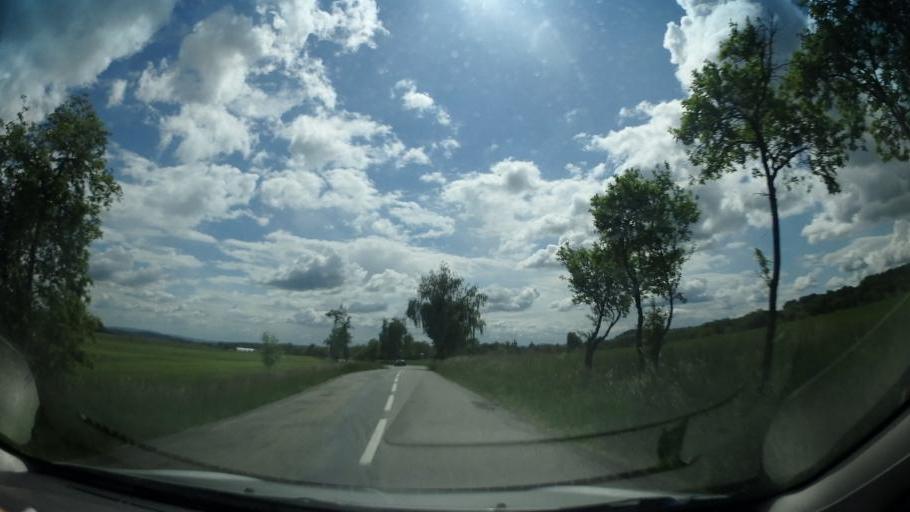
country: CZ
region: South Moravian
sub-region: Okres Blansko
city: Letovice
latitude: 49.5974
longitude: 16.5987
